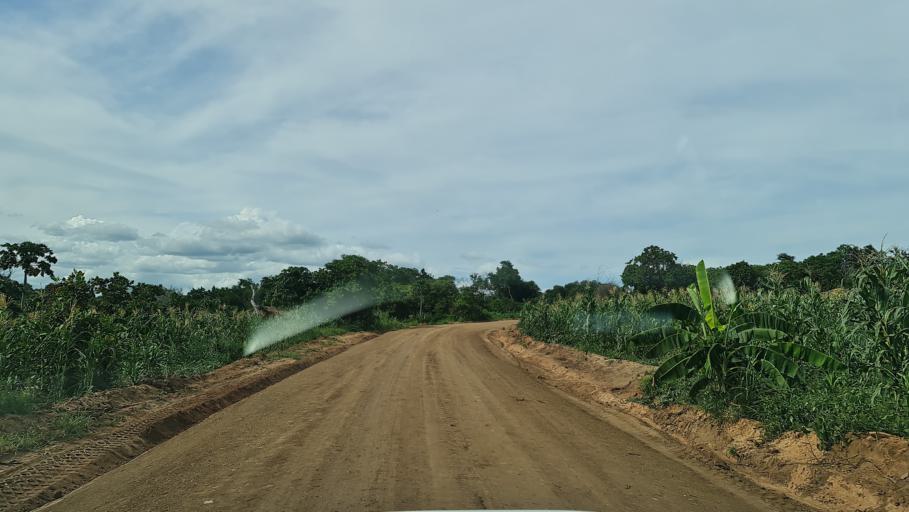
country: MZ
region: Nampula
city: Ilha de Mocambique
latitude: -14.8973
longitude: 40.4654
